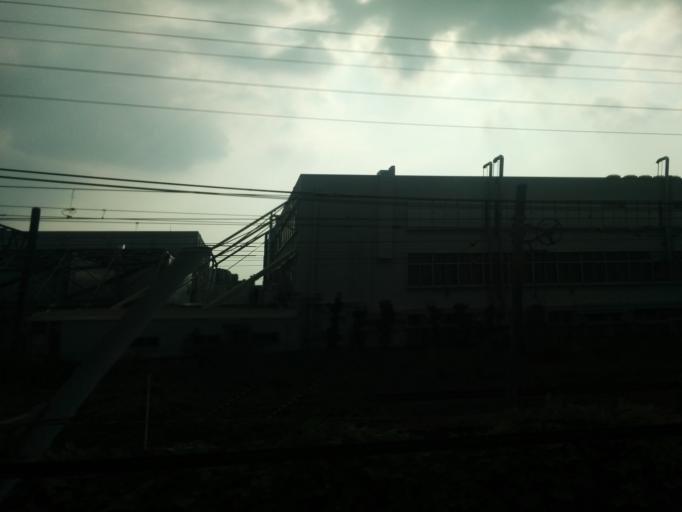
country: JP
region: Aichi
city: Nagoya-shi
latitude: 35.0892
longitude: 136.9297
